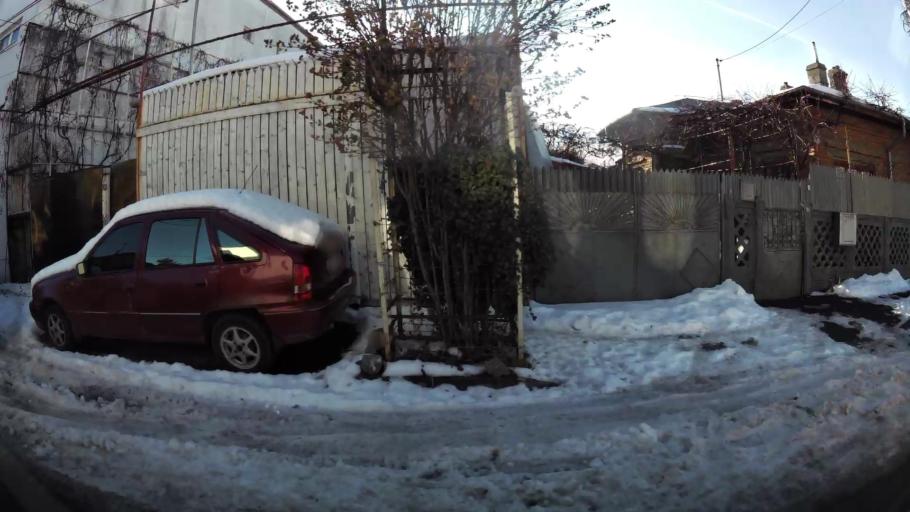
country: RO
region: Bucuresti
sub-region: Municipiul Bucuresti
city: Bucuresti
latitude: 44.4043
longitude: 26.0901
